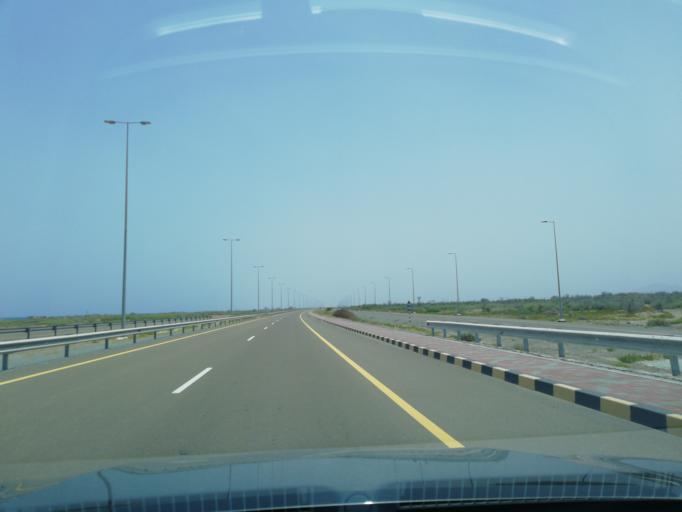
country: OM
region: Al Batinah
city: Shinas
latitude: 24.8916
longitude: 56.4006
